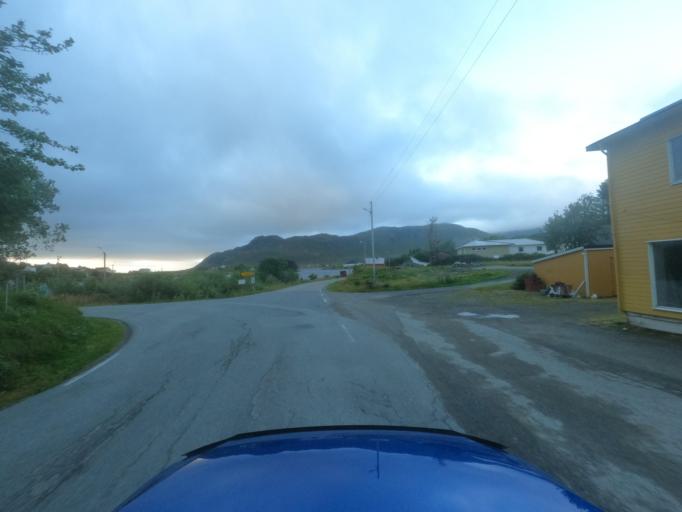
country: NO
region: Nordland
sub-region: Vestvagoy
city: Evjen
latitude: 68.2560
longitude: 13.7814
